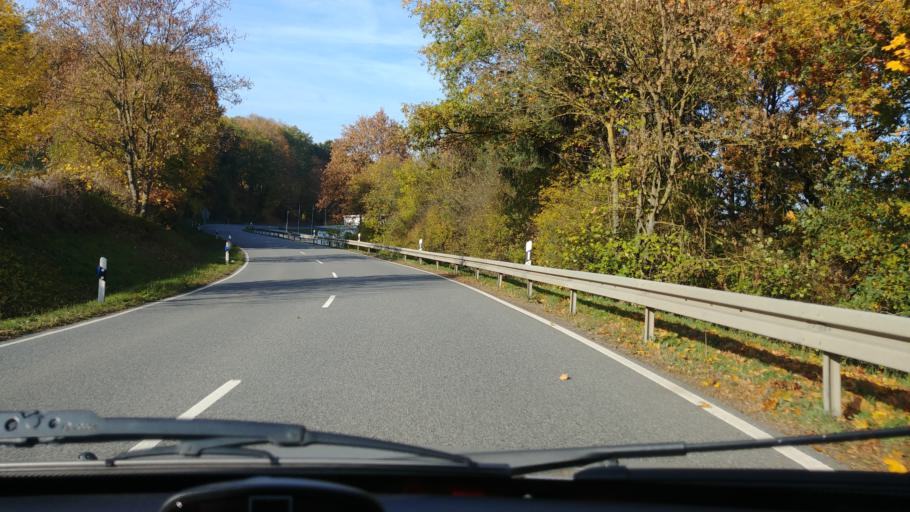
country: DE
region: Rheinland-Pfalz
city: Schiesheim
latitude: 50.2578
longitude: 8.0556
